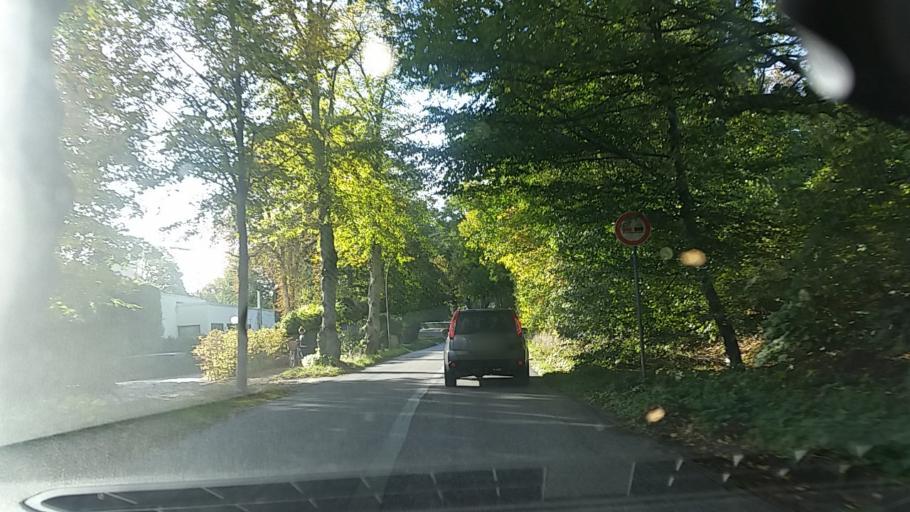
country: DE
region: Hamburg
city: Duvenstedt
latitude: 53.7070
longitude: 10.1201
